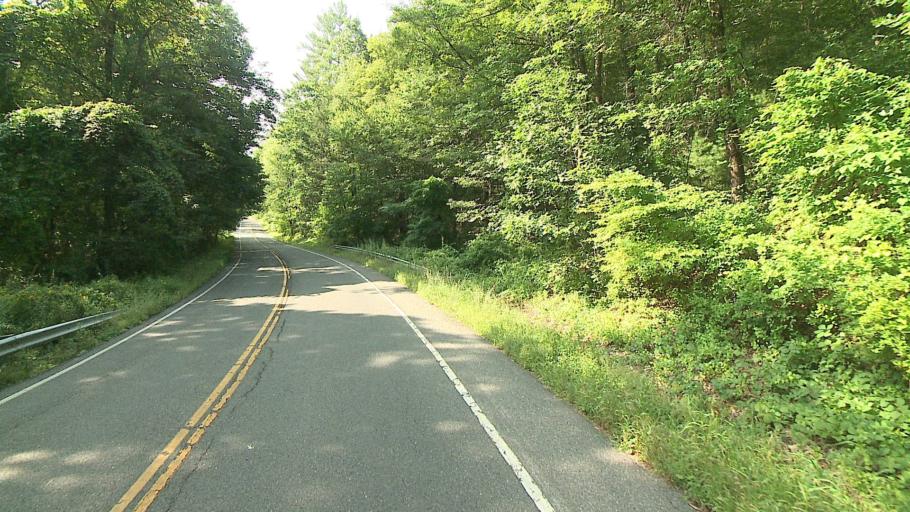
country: US
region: Connecticut
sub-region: Litchfield County
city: Kent
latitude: 41.8522
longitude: -73.3766
